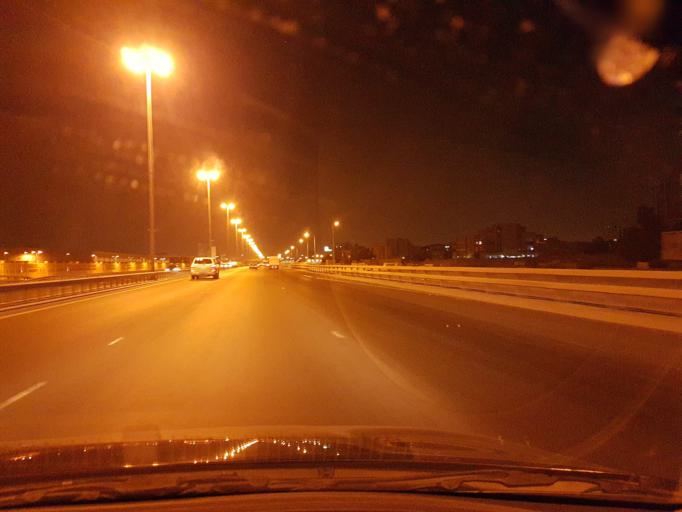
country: BH
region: Manama
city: Manama
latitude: 26.2123
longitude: 50.6197
